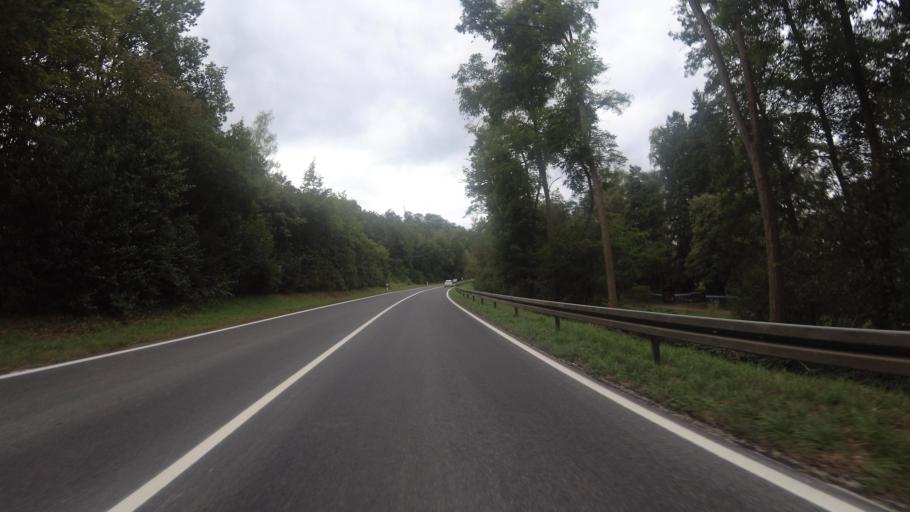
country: DE
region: Saarland
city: Quierschied
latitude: 49.3207
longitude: 7.0565
